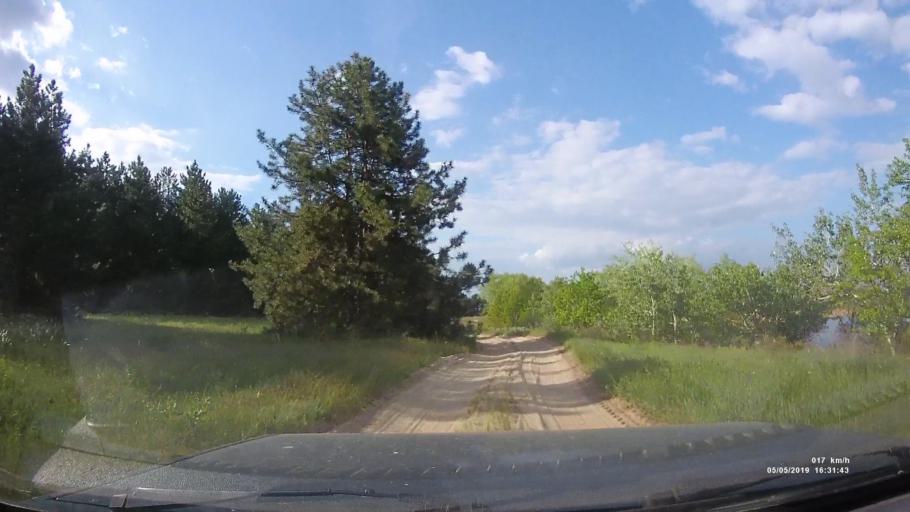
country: RU
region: Rostov
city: Ust'-Donetskiy
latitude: 47.7770
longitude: 41.0144
